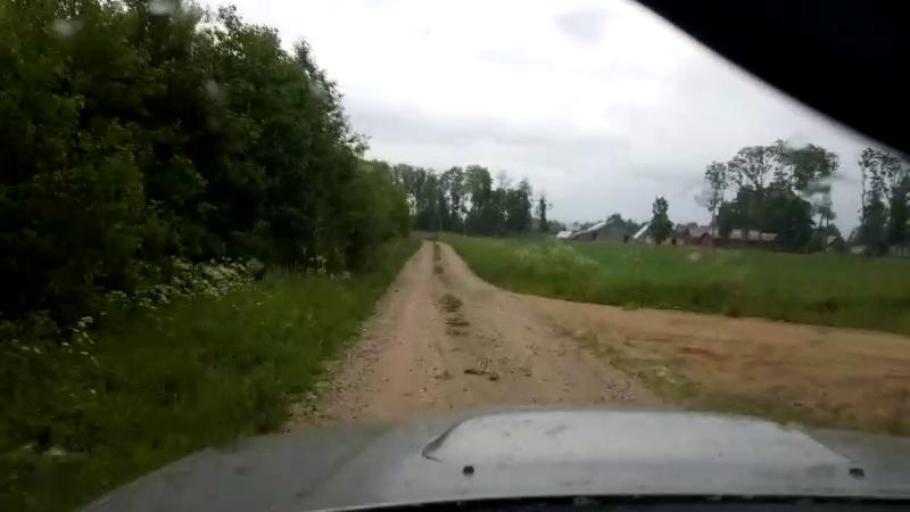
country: EE
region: Paernumaa
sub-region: Tootsi vald
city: Tootsi
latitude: 58.5849
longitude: 24.6537
